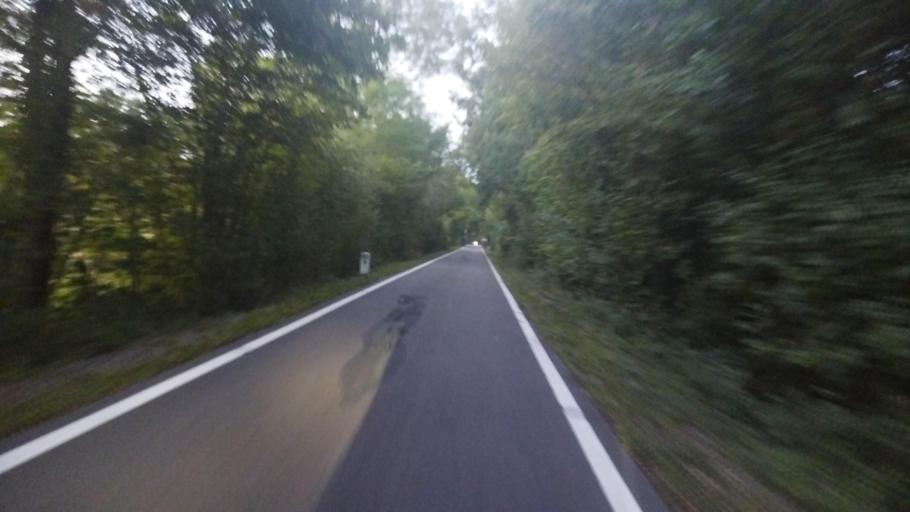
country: DE
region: North Rhine-Westphalia
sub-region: Regierungsbezirk Munster
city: Horstmar
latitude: 52.0985
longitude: 7.3306
